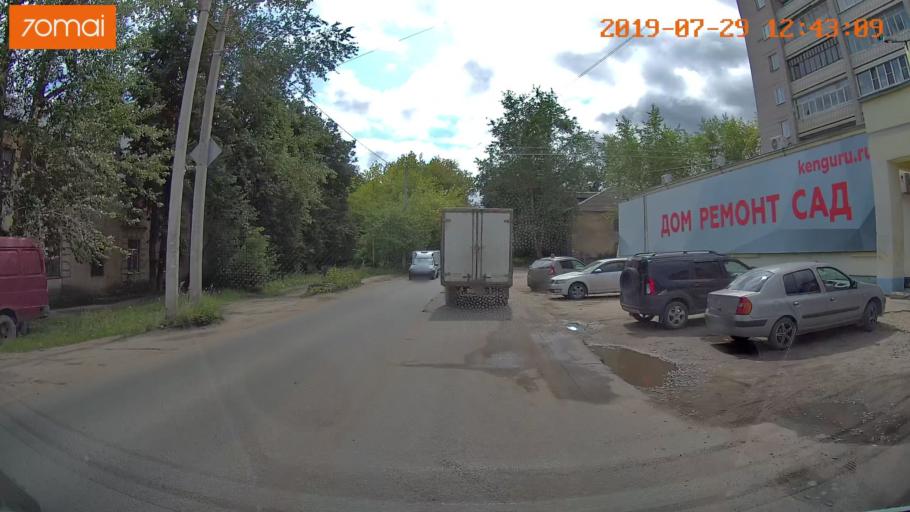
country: RU
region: Ivanovo
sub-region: Gorod Ivanovo
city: Ivanovo
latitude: 57.0037
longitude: 40.9308
